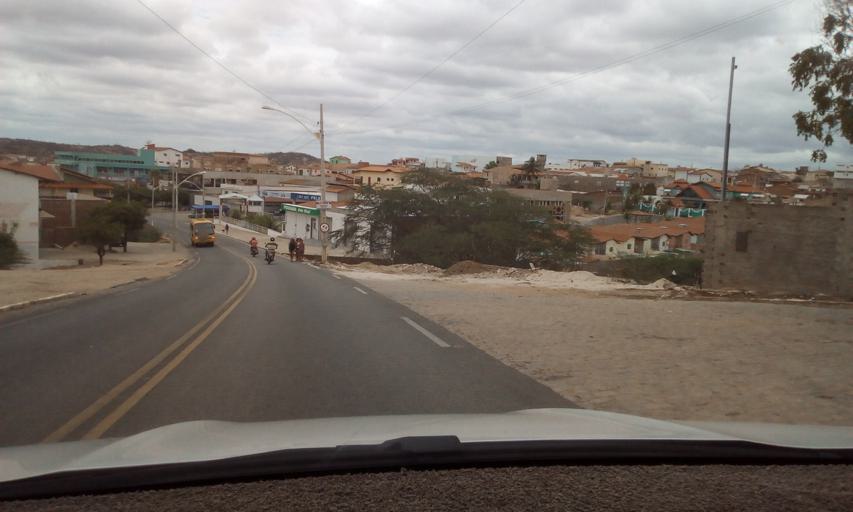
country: BR
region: Paraiba
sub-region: Picui
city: Picui
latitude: -6.5097
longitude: -36.3401
